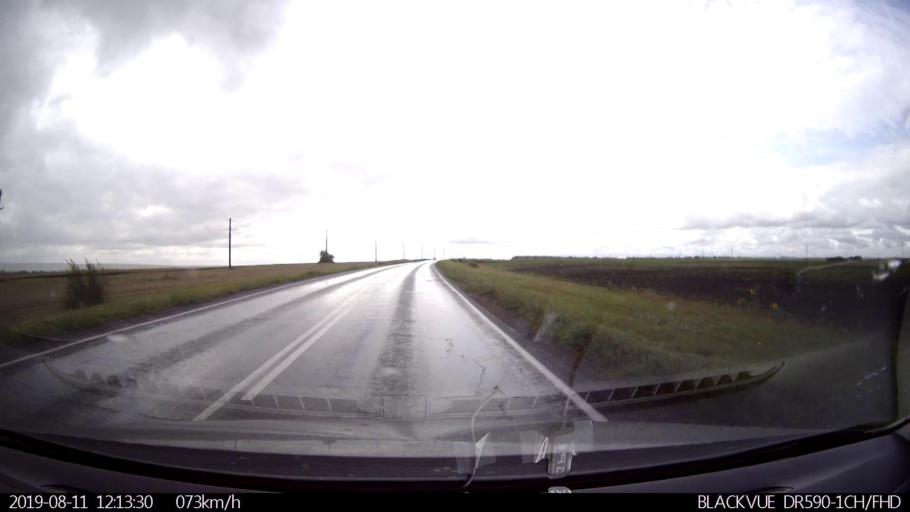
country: RU
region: Ulyanovsk
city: Silikatnyy
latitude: 53.9613
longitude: 47.9916
